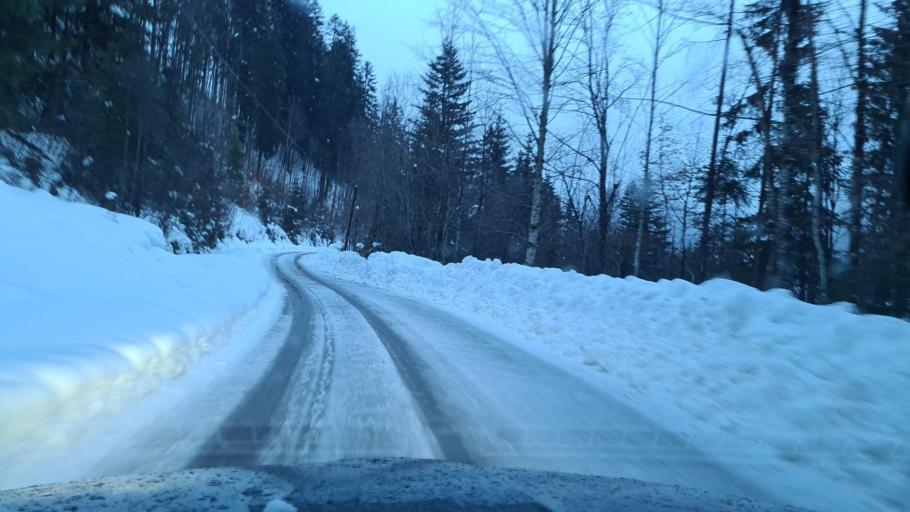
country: AT
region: Salzburg
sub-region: Politischer Bezirk Sankt Johann im Pongau
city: Werfen
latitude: 47.4864
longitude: 13.1566
